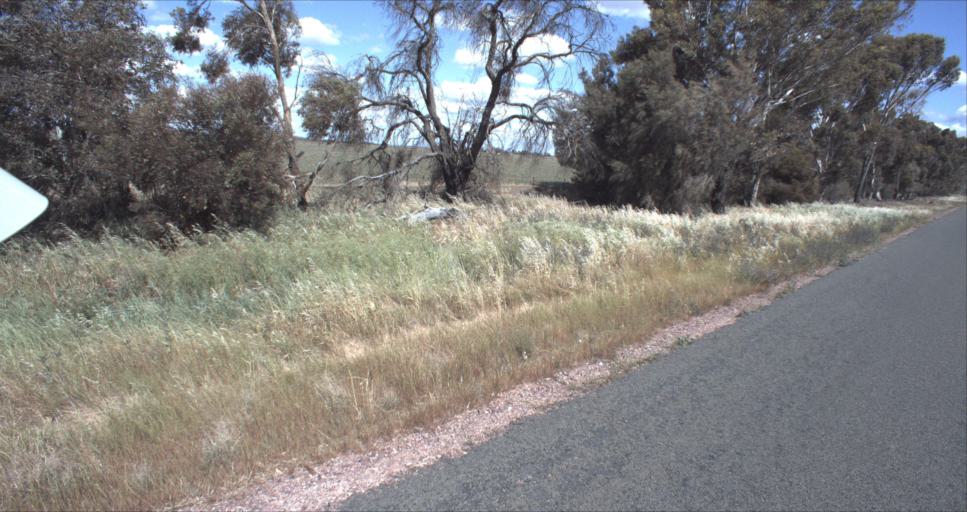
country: AU
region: New South Wales
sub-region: Leeton
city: Leeton
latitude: -34.4727
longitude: 146.2506
